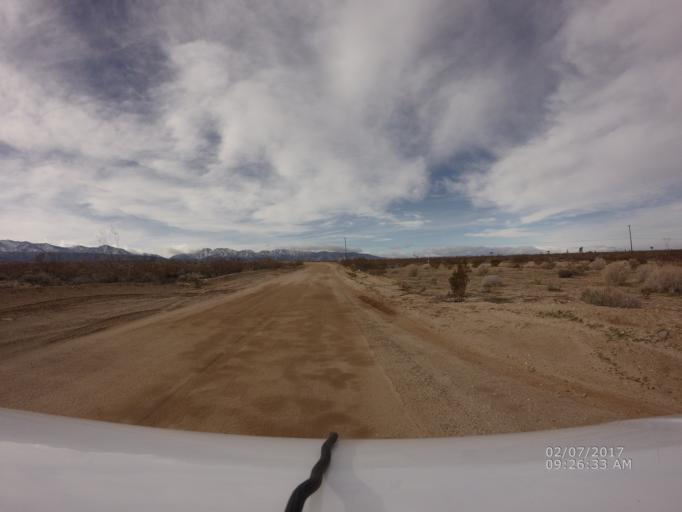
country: US
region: California
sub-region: Los Angeles County
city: Lake Los Angeles
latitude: 34.5020
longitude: -117.7642
